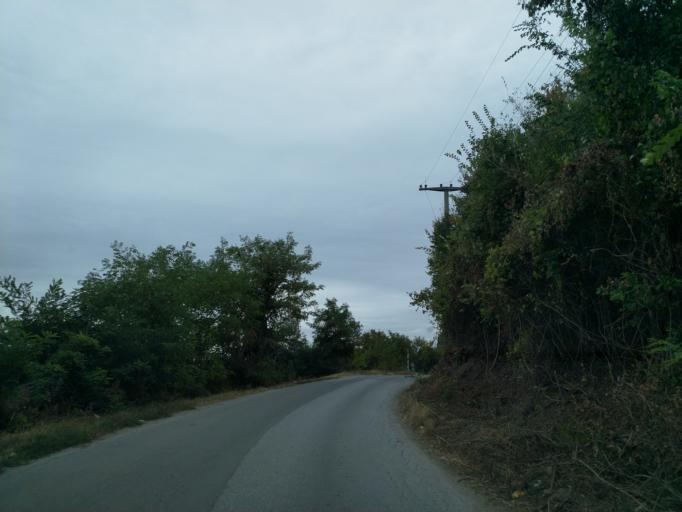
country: RS
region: Central Serbia
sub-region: Pomoravski Okrug
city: Cuprija
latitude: 43.8776
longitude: 21.3188
